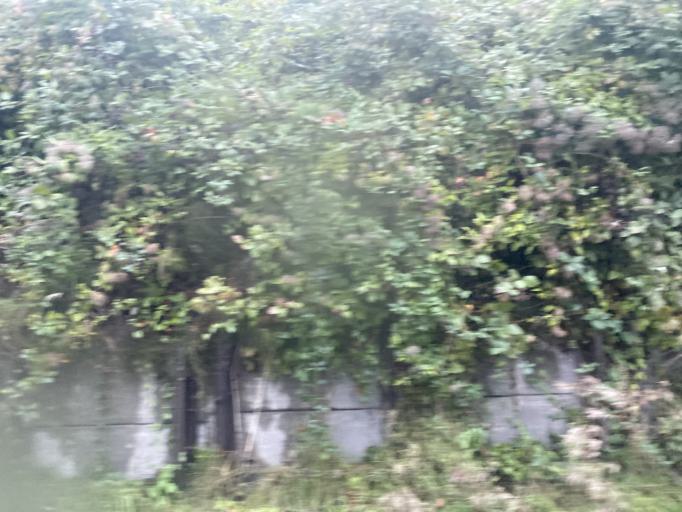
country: US
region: Washington
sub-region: King County
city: Seattle
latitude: 47.6426
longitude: -122.4161
